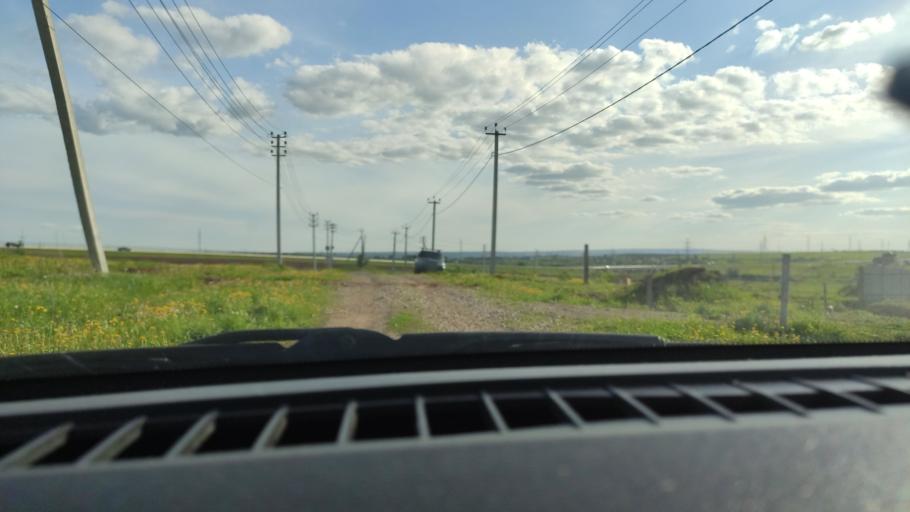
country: RU
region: Perm
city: Ferma
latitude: 57.9358
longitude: 56.3523
